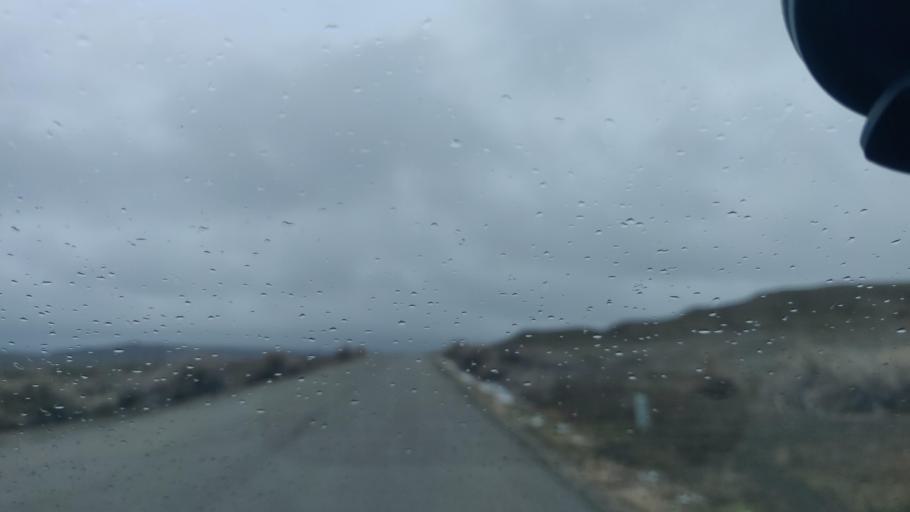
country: US
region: Colorado
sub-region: Mesa County
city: Clifton
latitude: 38.9436
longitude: -108.4037
